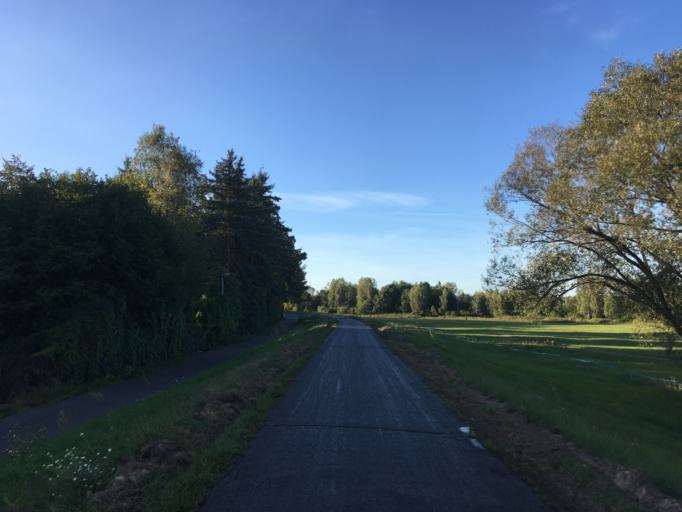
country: PL
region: Lubusz
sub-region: Powiat zarski
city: Trzebiel
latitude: 51.6744
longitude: 14.7465
